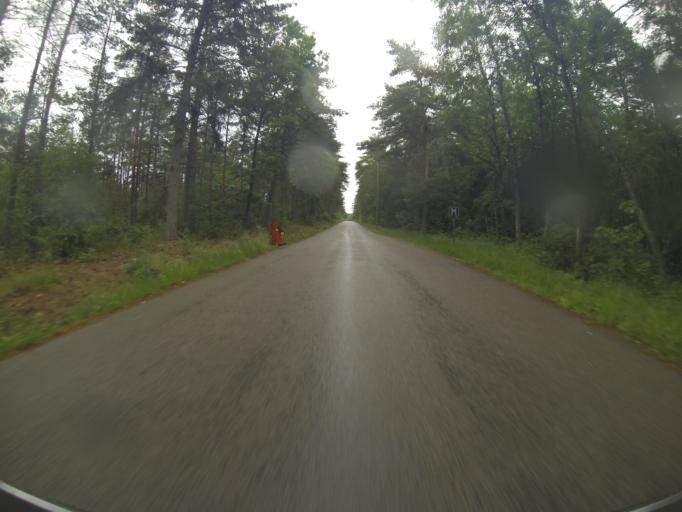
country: SE
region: Blekinge
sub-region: Ronneby Kommun
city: Ronneby
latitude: 56.1709
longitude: 15.3242
